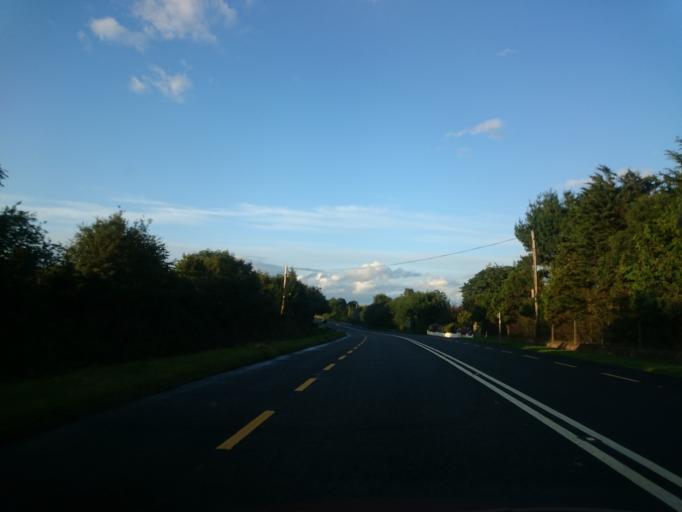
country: IE
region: Leinster
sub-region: Loch Garman
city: Ferns
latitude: 52.6262
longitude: -6.3988
